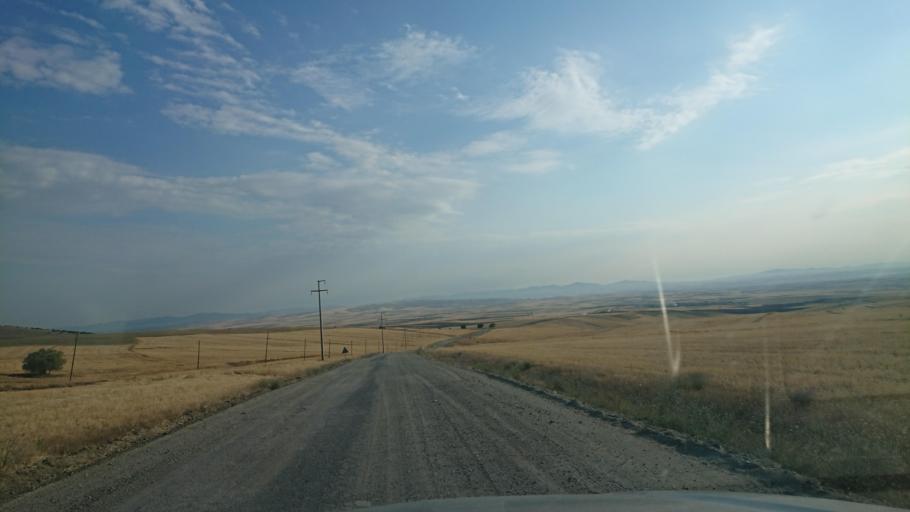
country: TR
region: Aksaray
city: Ortakoy
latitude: 38.7865
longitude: 34.0634
